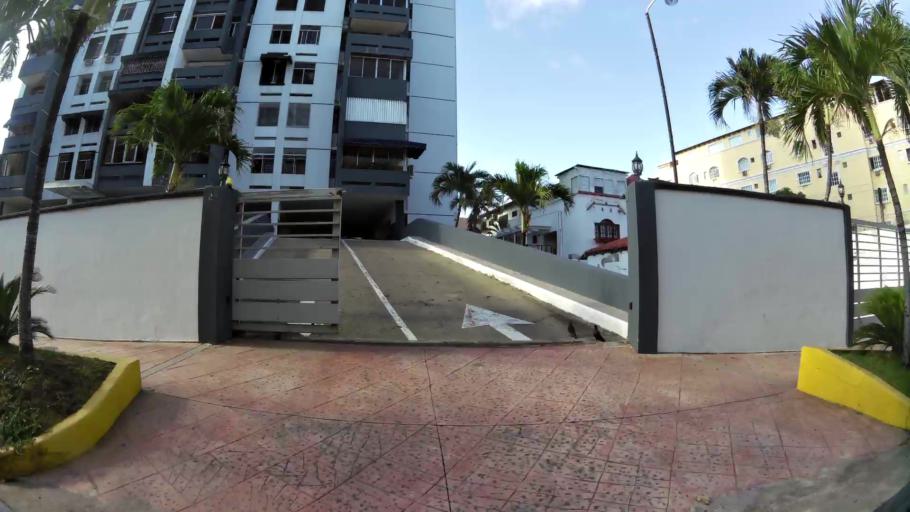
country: DO
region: Nacional
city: Ciudad Nueva
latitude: 18.4563
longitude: -69.9155
